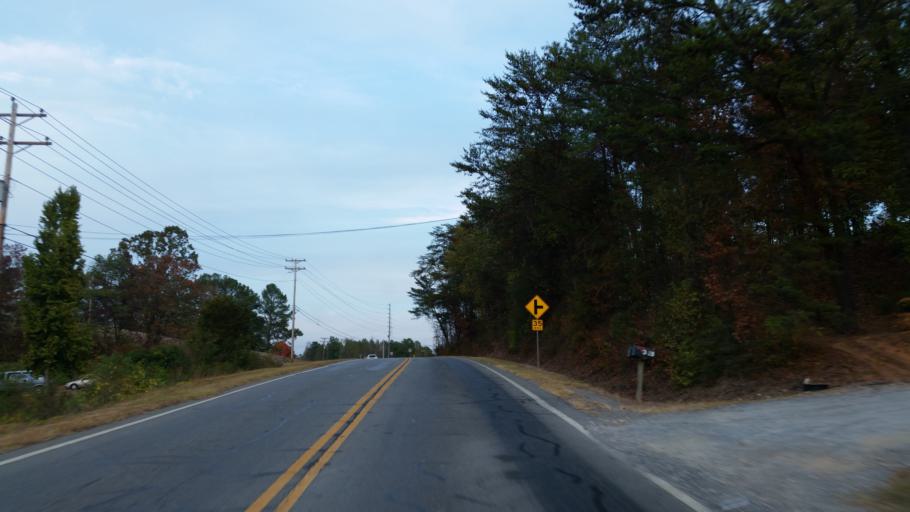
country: US
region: Georgia
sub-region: Gordon County
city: Calhoun
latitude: 34.5849
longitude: -84.9384
